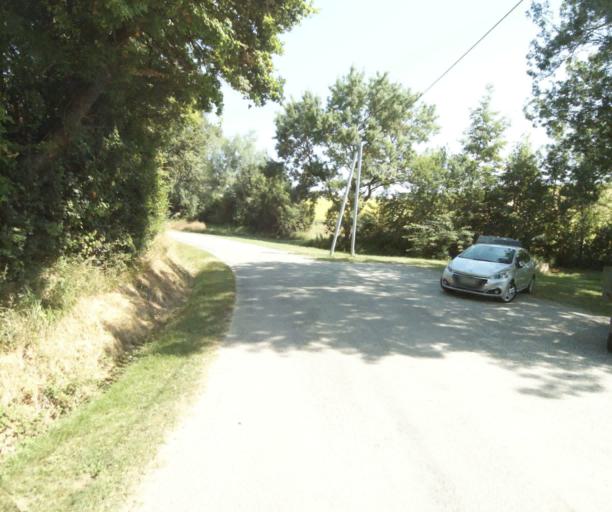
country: FR
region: Midi-Pyrenees
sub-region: Departement de la Haute-Garonne
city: Saint-Felix-Lauragais
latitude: 43.4563
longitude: 1.8415
